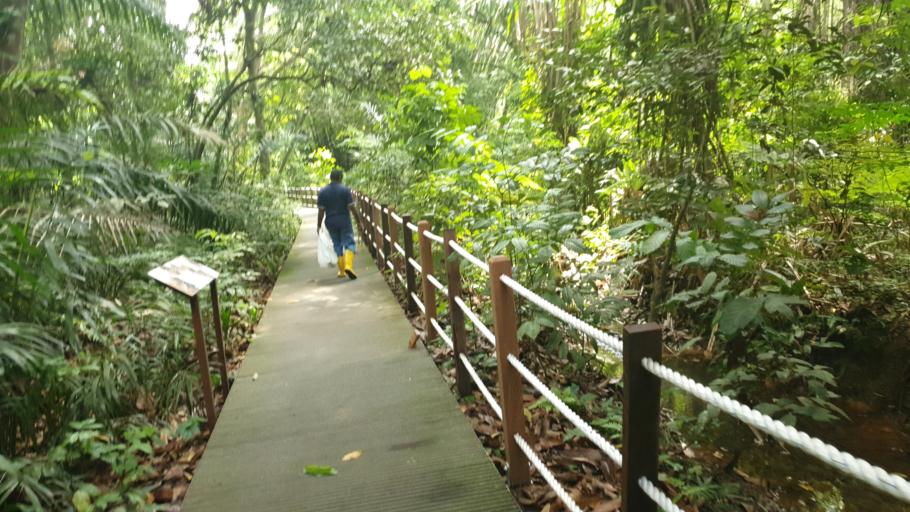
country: SG
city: Singapore
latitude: 1.3605
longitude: 103.8240
